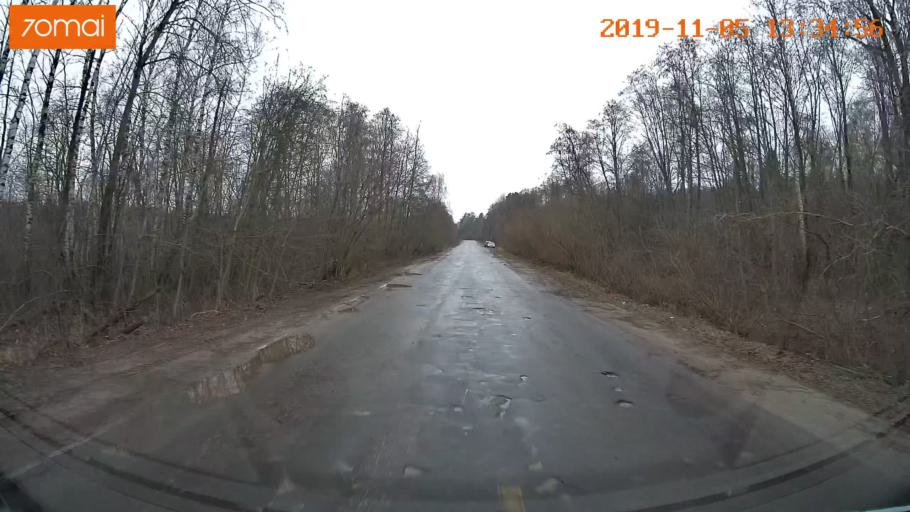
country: RU
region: Ivanovo
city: Shuya
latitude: 56.9043
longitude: 41.3893
